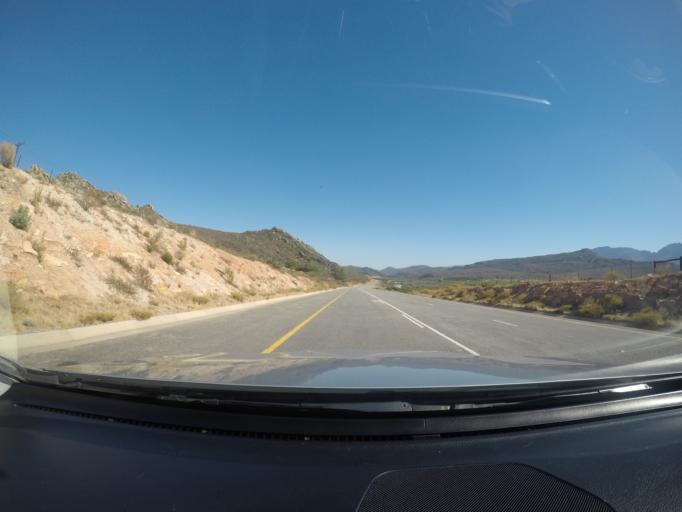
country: ZA
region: Western Cape
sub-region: West Coast District Municipality
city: Clanwilliam
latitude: -32.4503
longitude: 18.9590
